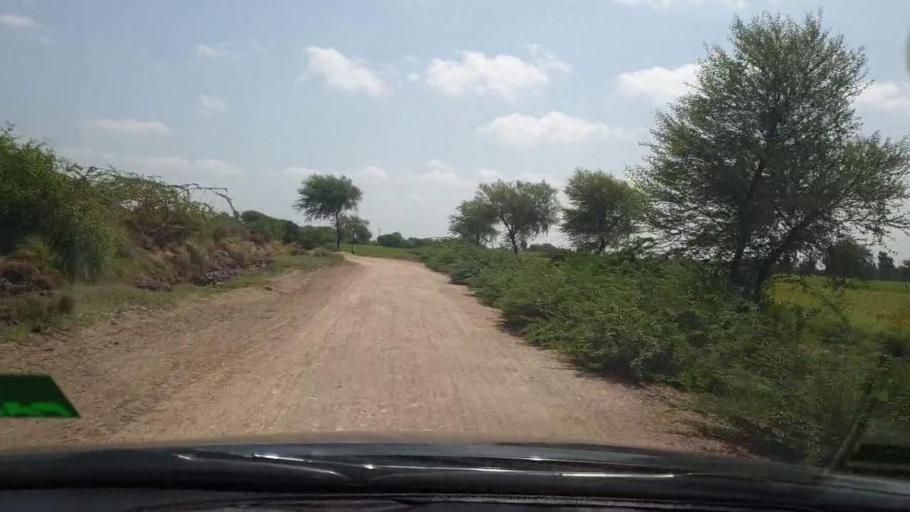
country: PK
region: Sindh
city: Tando Bago
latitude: 24.8761
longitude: 69.0834
